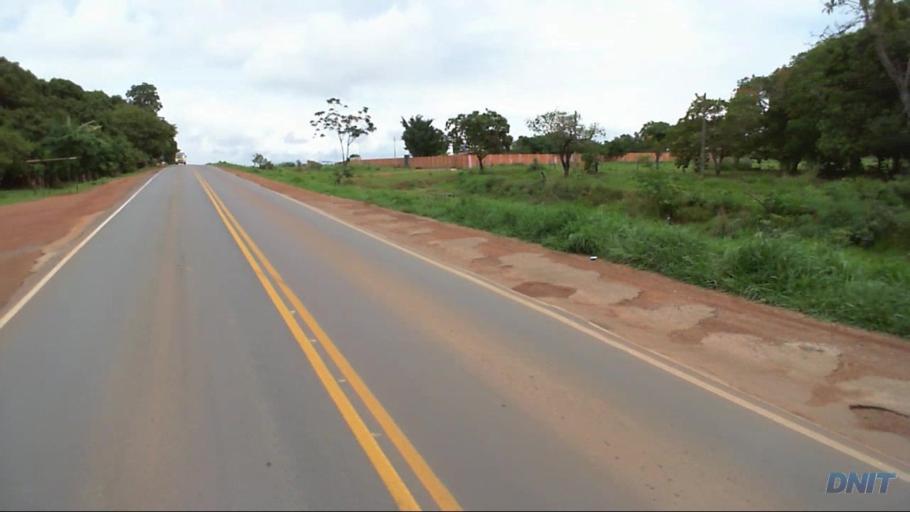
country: BR
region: Goias
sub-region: Padre Bernardo
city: Padre Bernardo
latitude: -15.3606
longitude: -48.2251
